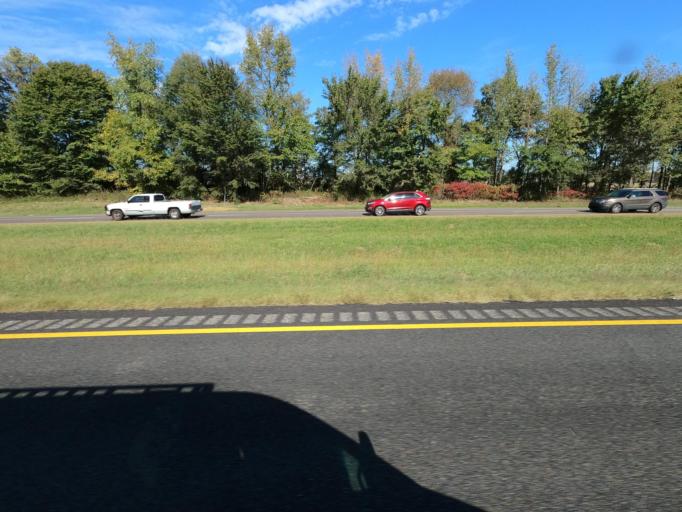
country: US
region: Tennessee
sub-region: Tipton County
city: Mason
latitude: 35.3736
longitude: -89.4629
